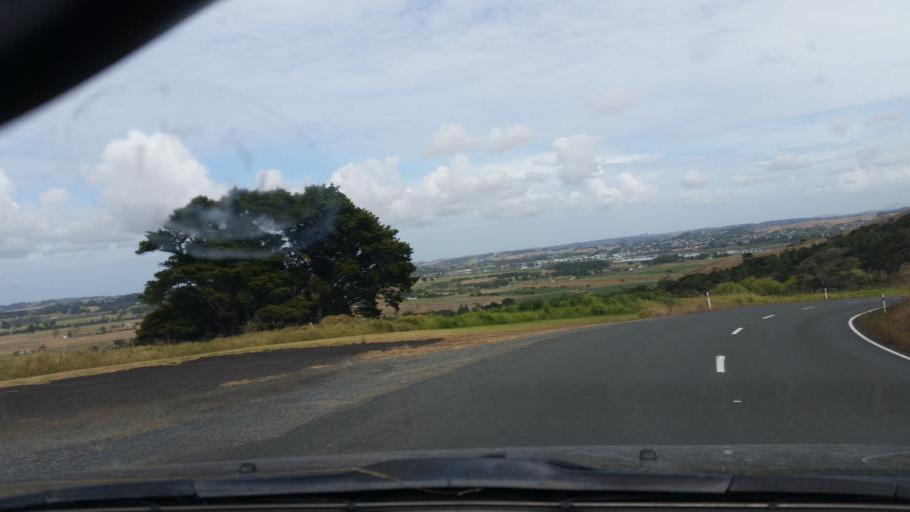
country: NZ
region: Northland
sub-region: Kaipara District
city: Dargaville
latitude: -35.9491
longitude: 173.9079
